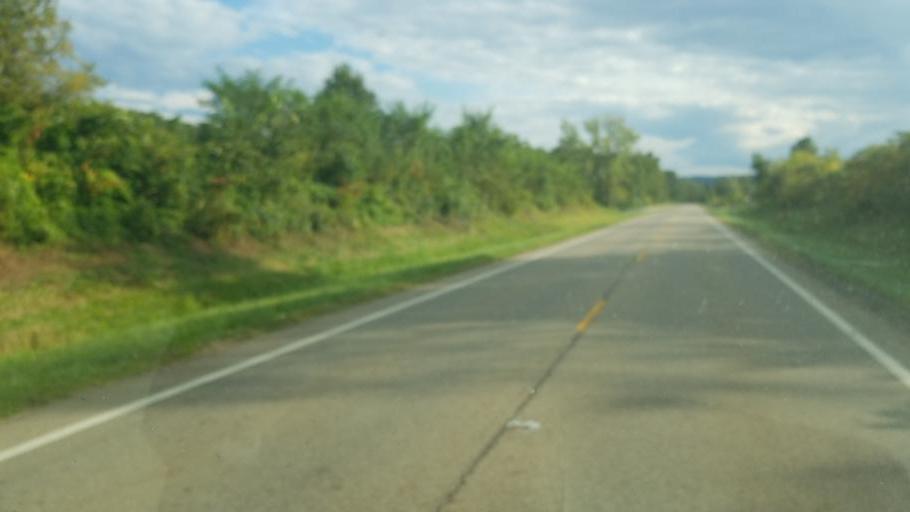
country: US
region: Ohio
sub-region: Holmes County
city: Millersburg
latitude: 40.4931
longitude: -81.9787
